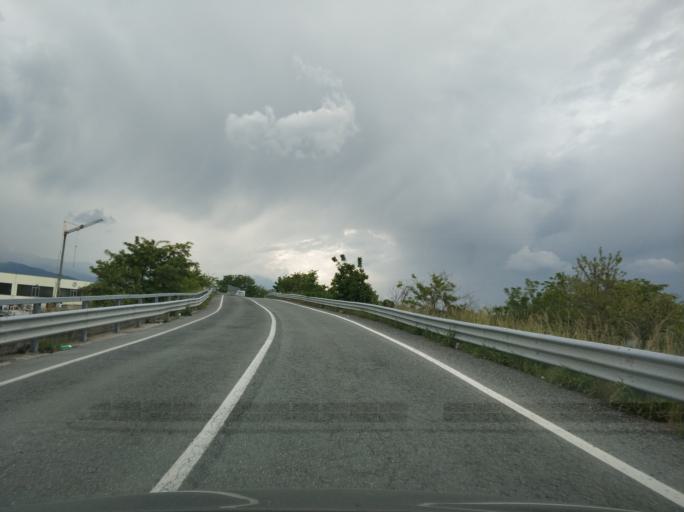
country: IT
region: Piedmont
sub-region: Provincia di Torino
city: San Maurizio
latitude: 45.2204
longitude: 7.6192
